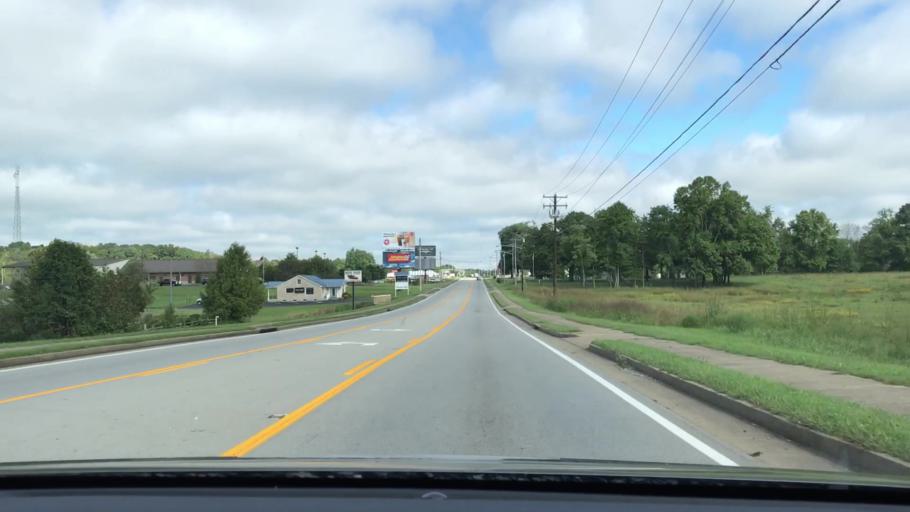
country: US
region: Kentucky
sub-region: Russell County
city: Jamestown
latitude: 37.0153
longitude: -85.0758
